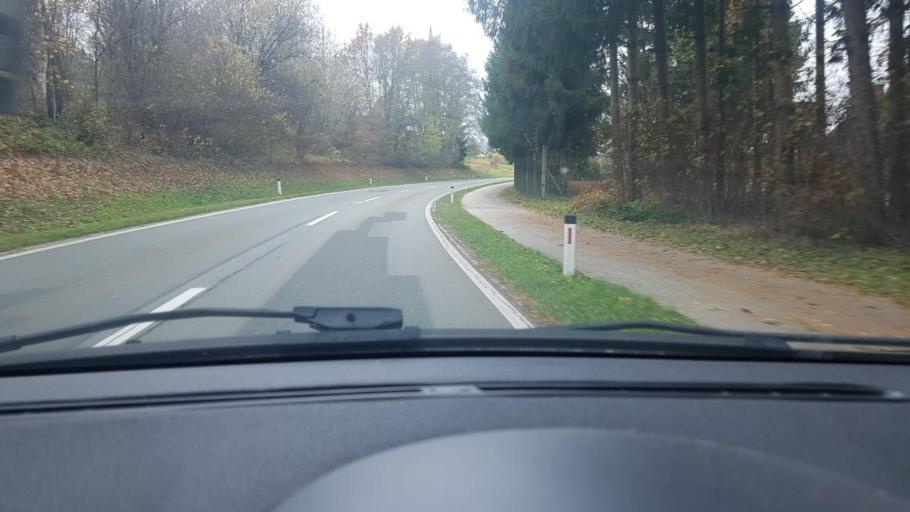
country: AT
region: Carinthia
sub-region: Politischer Bezirk Wolfsberg
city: Lavamund
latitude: 46.6420
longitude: 14.9371
